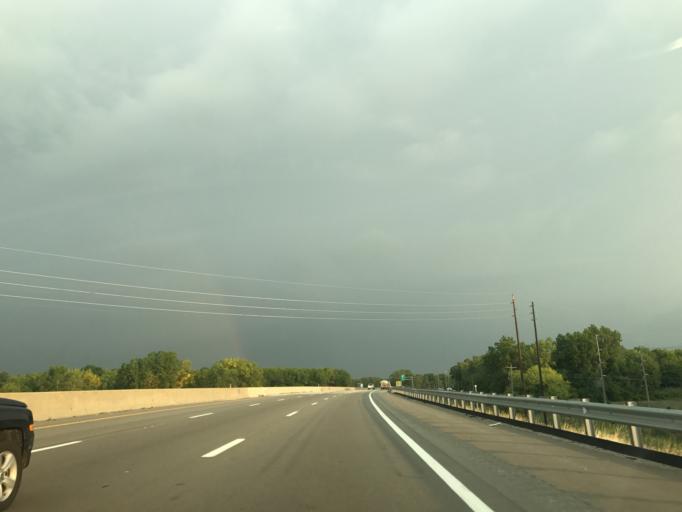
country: US
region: Ohio
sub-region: Lorain County
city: Elyria
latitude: 41.3813
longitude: -82.0673
